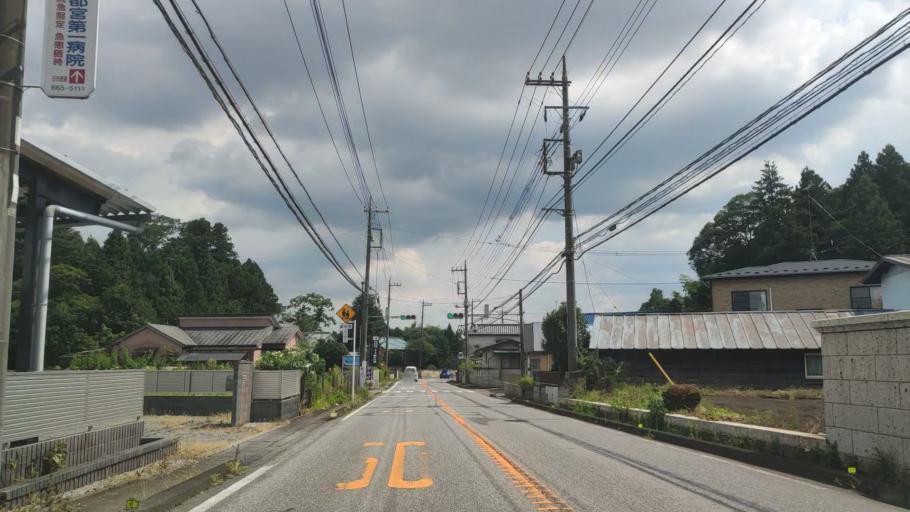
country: JP
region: Tochigi
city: Utsunomiya-shi
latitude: 36.6489
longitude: 139.8454
